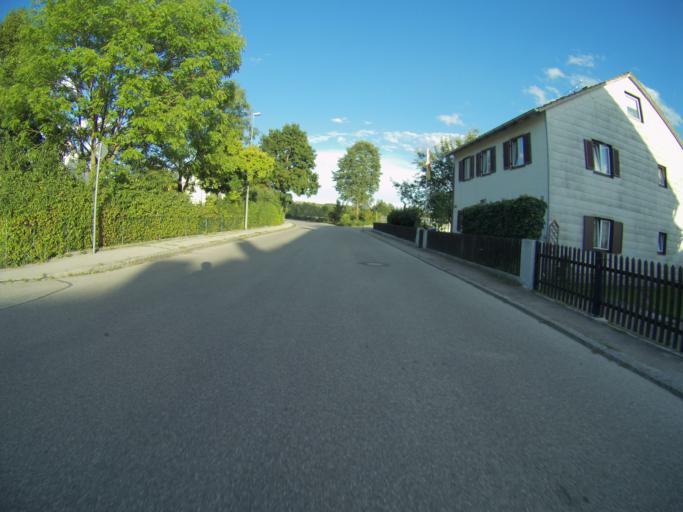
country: DE
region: Bavaria
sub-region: Upper Bavaria
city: Moosburg
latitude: 48.4572
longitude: 11.9293
